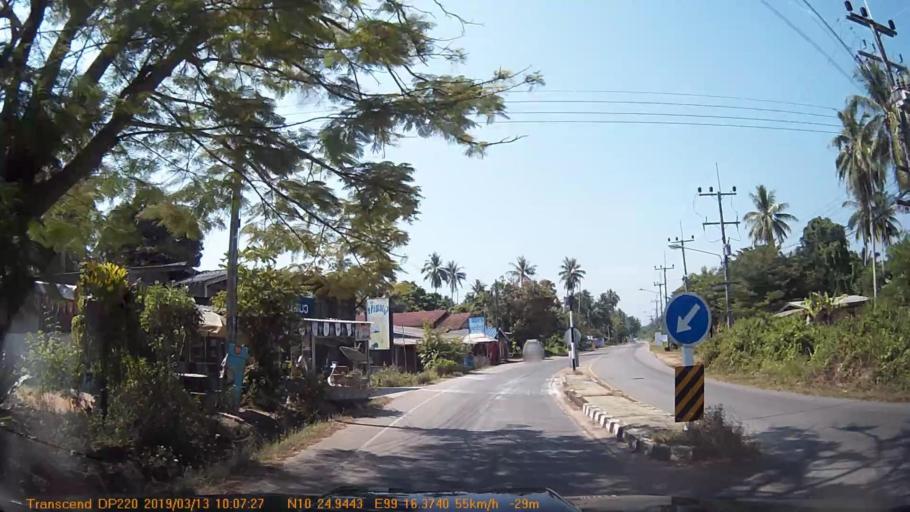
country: TH
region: Chumphon
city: Chumphon
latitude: 10.4155
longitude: 99.2729
